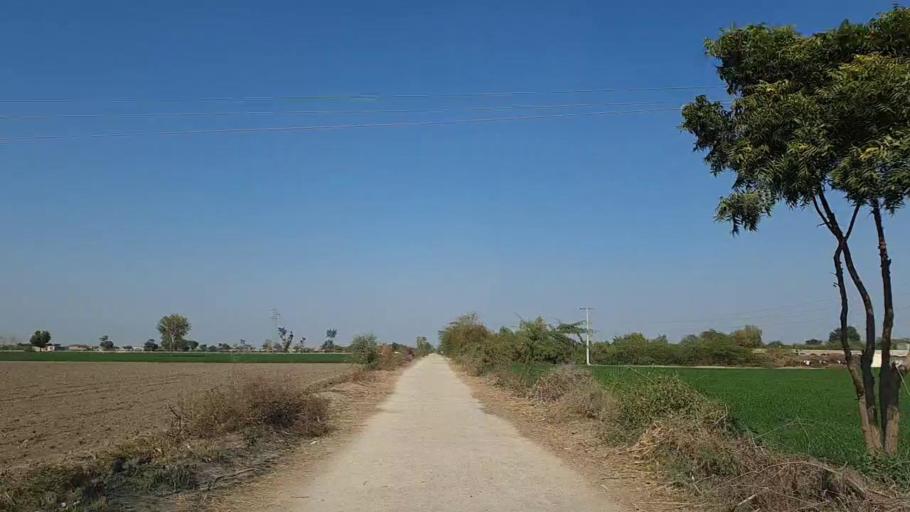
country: PK
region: Sindh
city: Nawabshah
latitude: 26.2489
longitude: 68.4410
